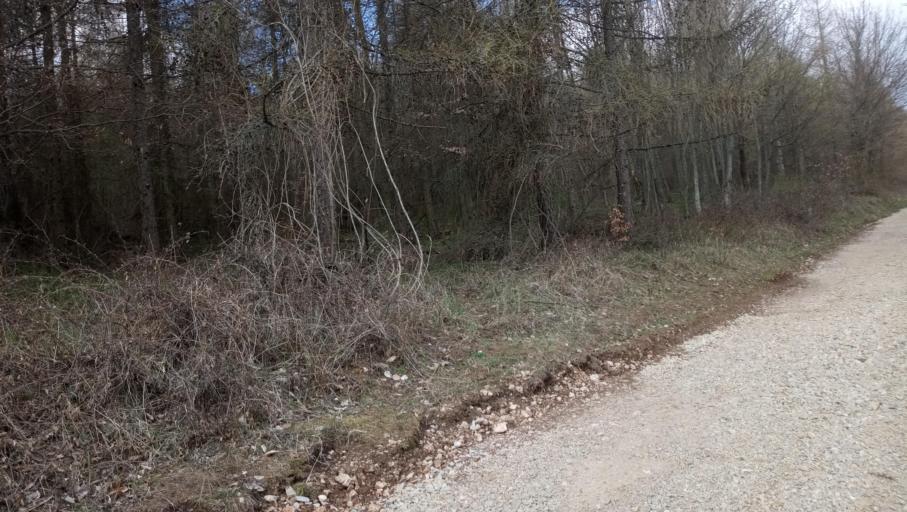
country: HU
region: Veszprem
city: Herend
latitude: 47.1963
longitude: 17.7571
